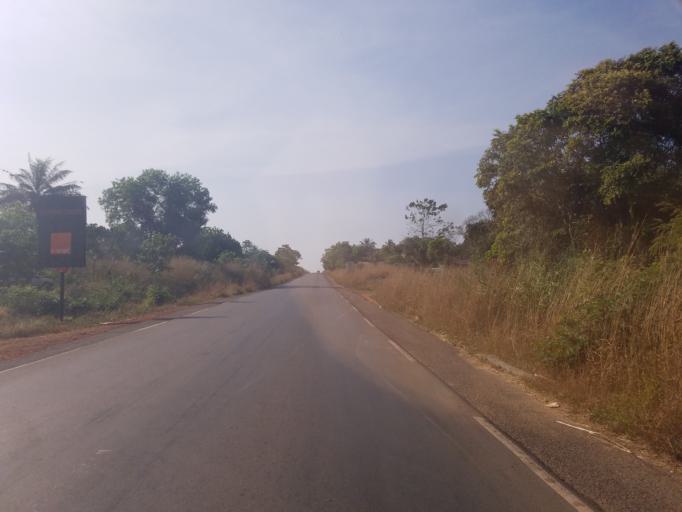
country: GN
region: Boke
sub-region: Boffa
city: Boffa
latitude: 10.1885
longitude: -14.0474
